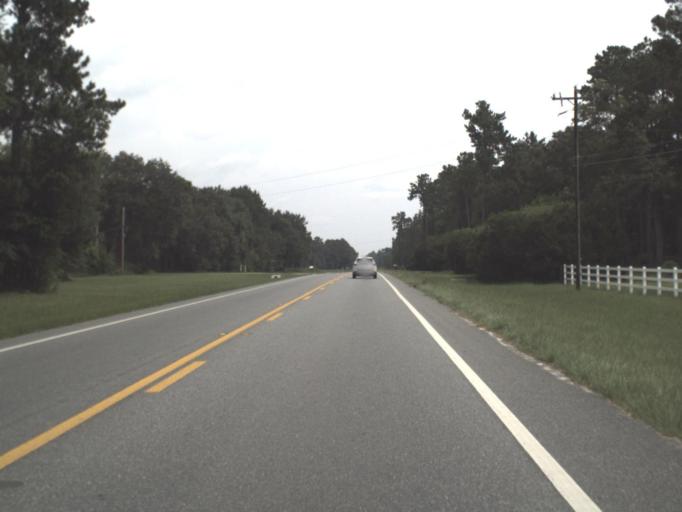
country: US
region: Florida
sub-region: Columbia County
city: Watertown
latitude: 30.0517
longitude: -82.5988
